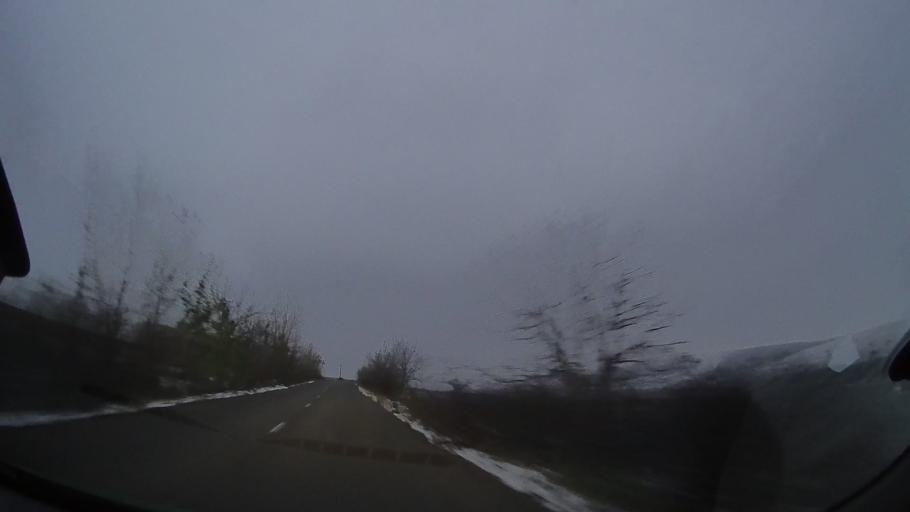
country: RO
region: Vaslui
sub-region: Comuna Gagesti
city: Gagesti
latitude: 46.3976
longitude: 27.9816
